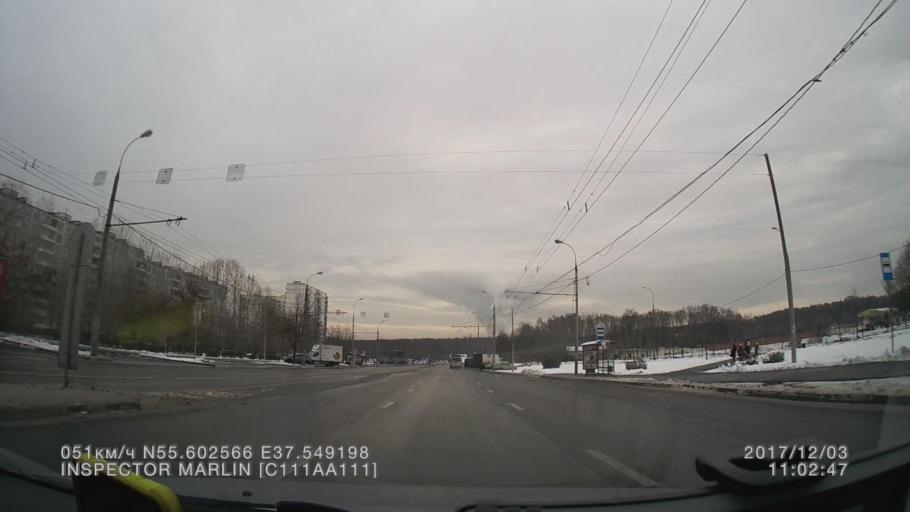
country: RU
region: Moscow
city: Yasenevo
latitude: 55.6025
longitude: 37.5493
